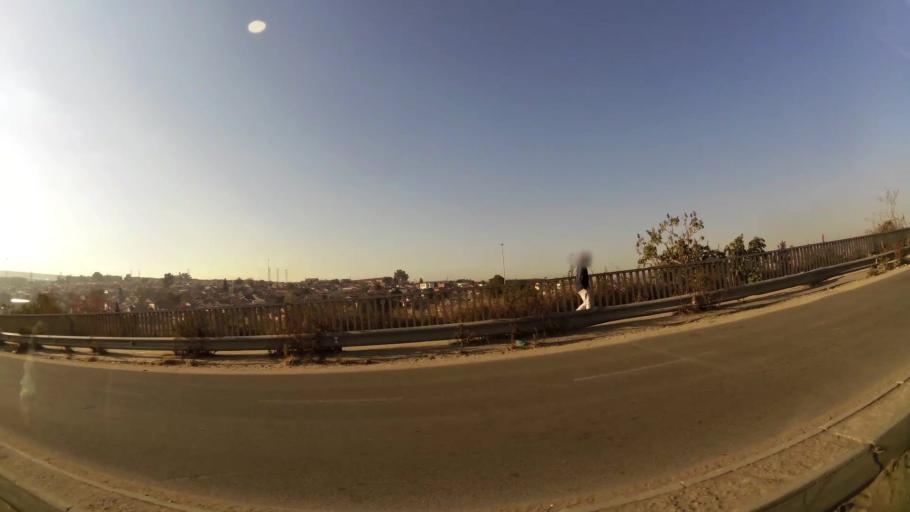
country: ZA
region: Gauteng
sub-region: City of Johannesburg Metropolitan Municipality
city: Modderfontein
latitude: -26.0956
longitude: 28.1044
